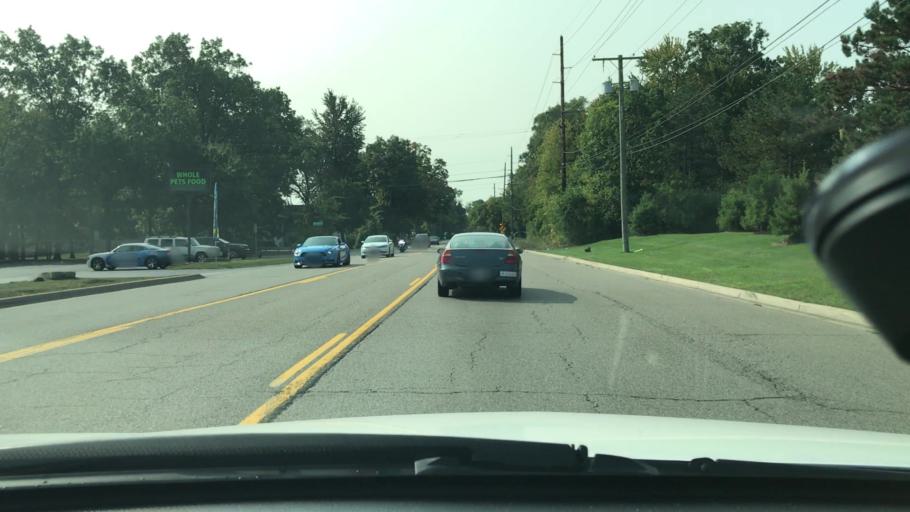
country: US
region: Michigan
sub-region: Oakland County
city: Wolverine Lake
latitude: 42.5898
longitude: -83.4459
